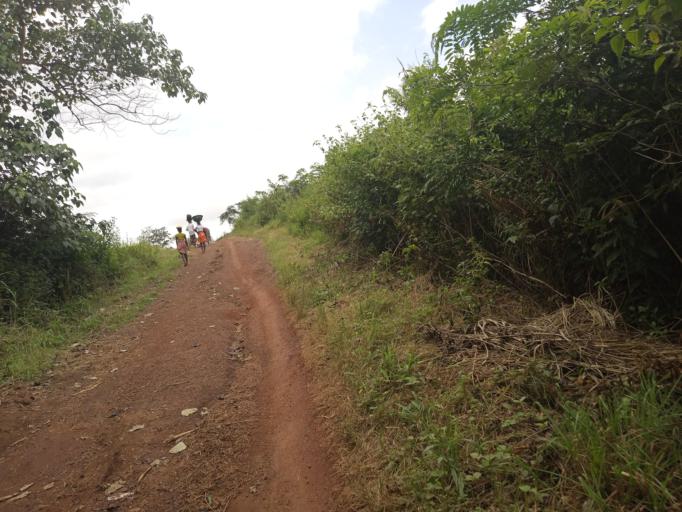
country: SL
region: Northern Province
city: Kamakwie
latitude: 9.4817
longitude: -12.2506
